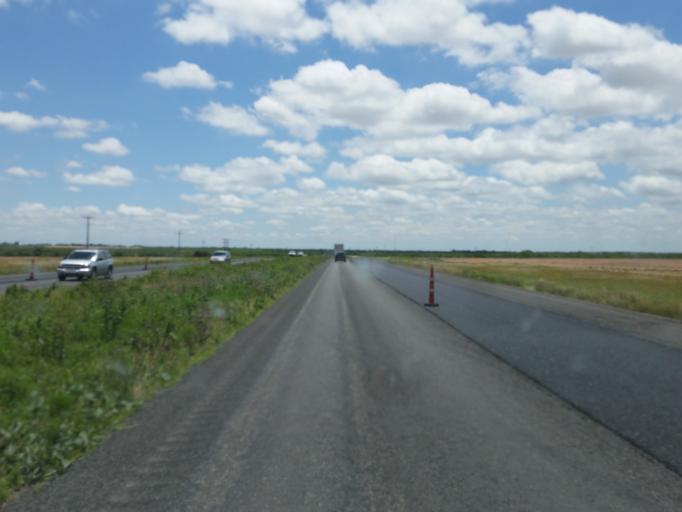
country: US
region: Texas
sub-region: Scurry County
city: Snyder
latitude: 32.7758
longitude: -100.9418
